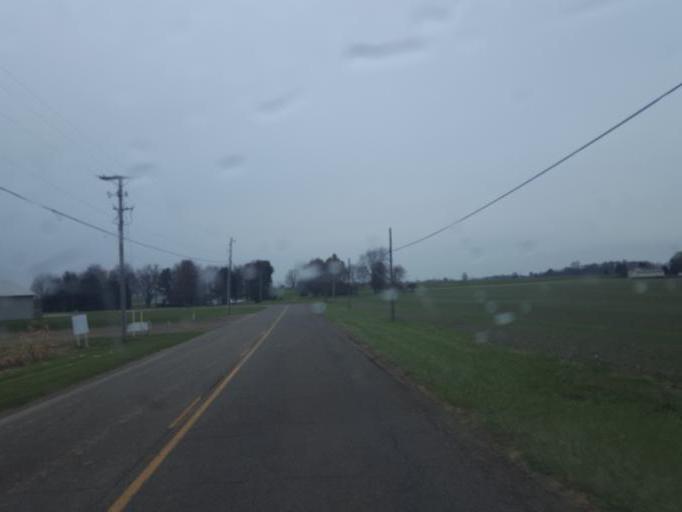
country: US
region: Ohio
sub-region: Knox County
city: Fredericktown
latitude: 40.5159
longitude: -82.5488
